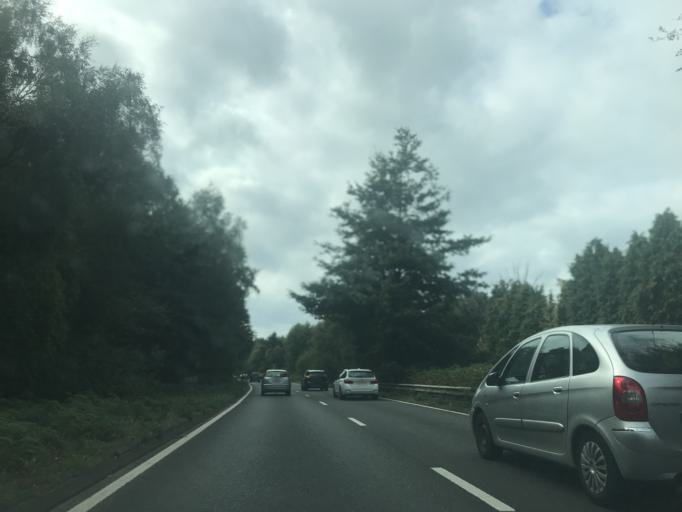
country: GB
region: England
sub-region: Surrey
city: Bagshot
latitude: 51.3719
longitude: -0.6901
